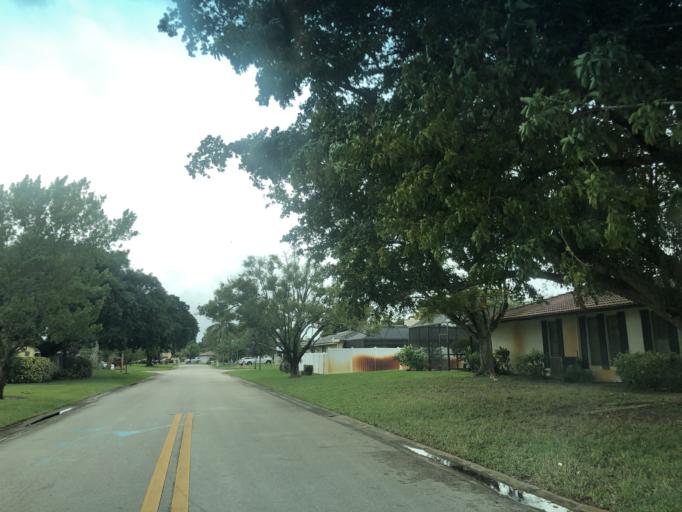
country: US
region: Florida
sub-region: Broward County
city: North Lauderdale
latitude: 26.2427
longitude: -80.2397
